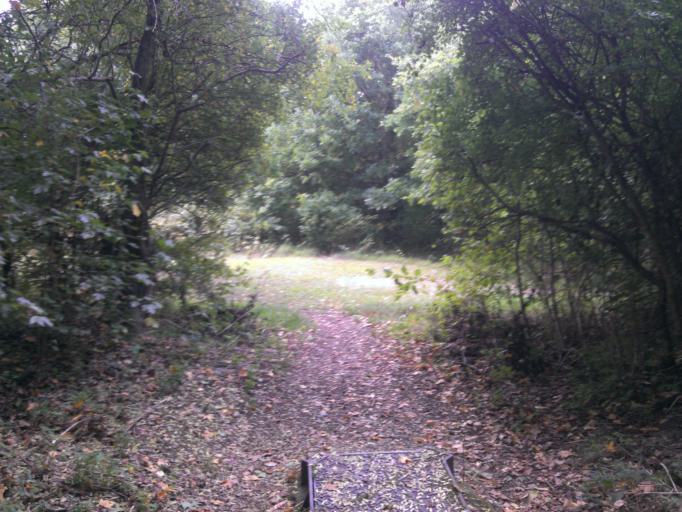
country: GB
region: England
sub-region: Essex
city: Rowhedge
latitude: 51.8681
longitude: 0.9508
